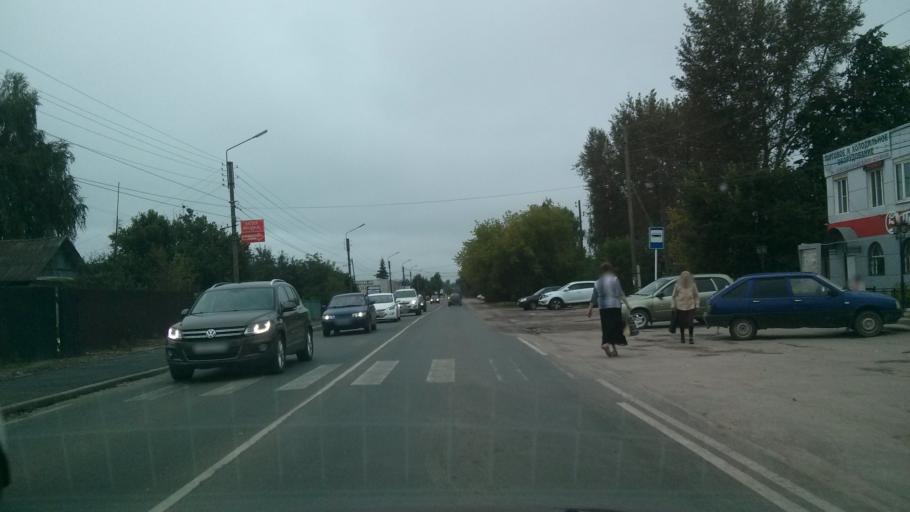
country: RU
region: Vladimir
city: Murom
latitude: 55.5928
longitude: 42.0346
